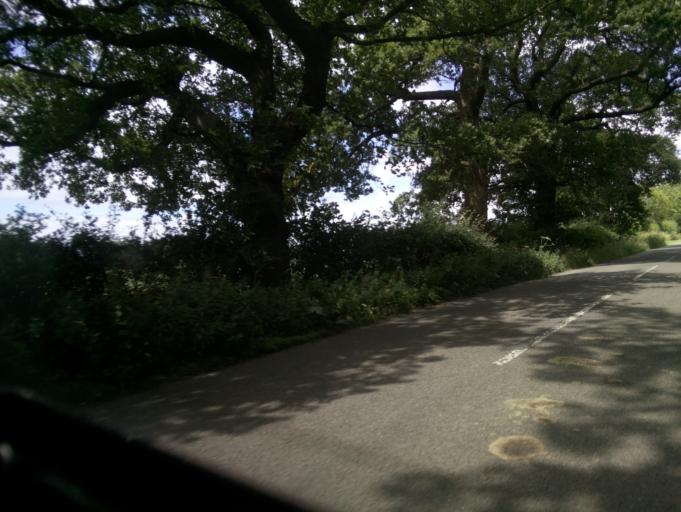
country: GB
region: England
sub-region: Nottinghamshire
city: Cotgrave
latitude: 52.8556
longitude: -1.0692
